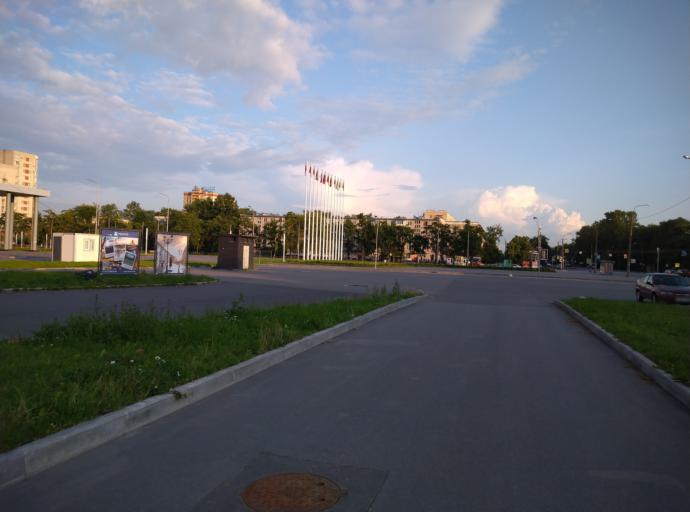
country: RU
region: St.-Petersburg
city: Kupchino
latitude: 59.8658
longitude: 30.3375
